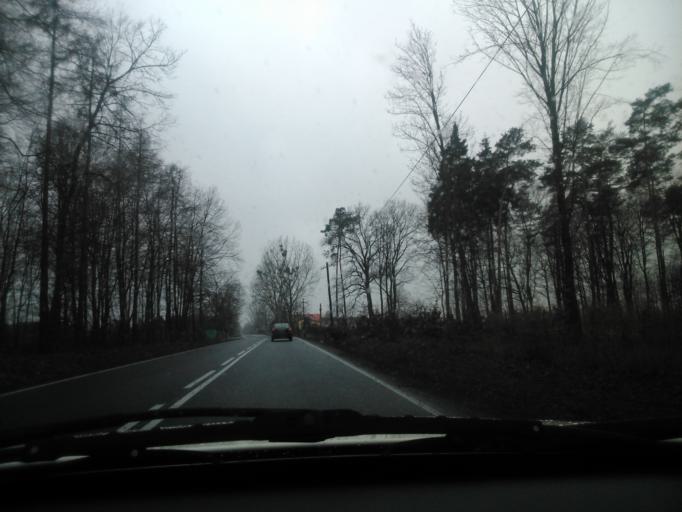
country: PL
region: Kujawsko-Pomorskie
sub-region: Powiat brodnicki
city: Bobrowo
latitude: 53.2548
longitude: 19.3195
